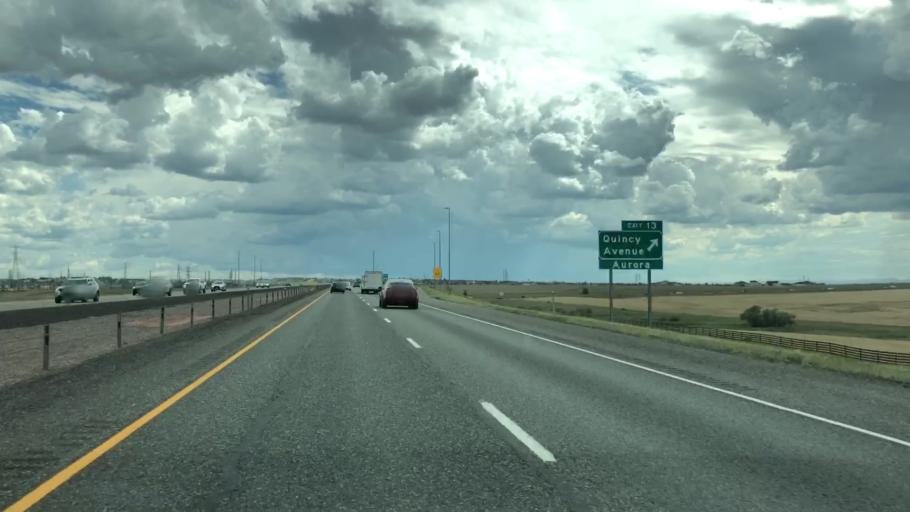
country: US
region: Colorado
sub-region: Arapahoe County
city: Dove Valley
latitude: 39.6450
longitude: -104.7192
